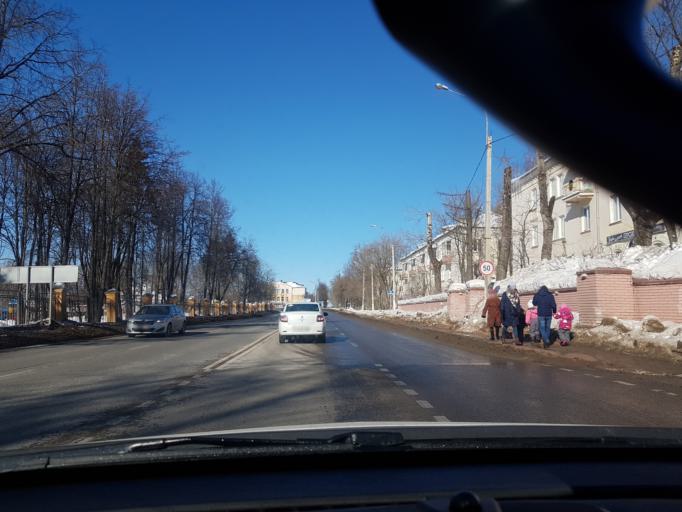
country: RU
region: Moskovskaya
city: Istra
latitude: 55.9180
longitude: 36.8586
